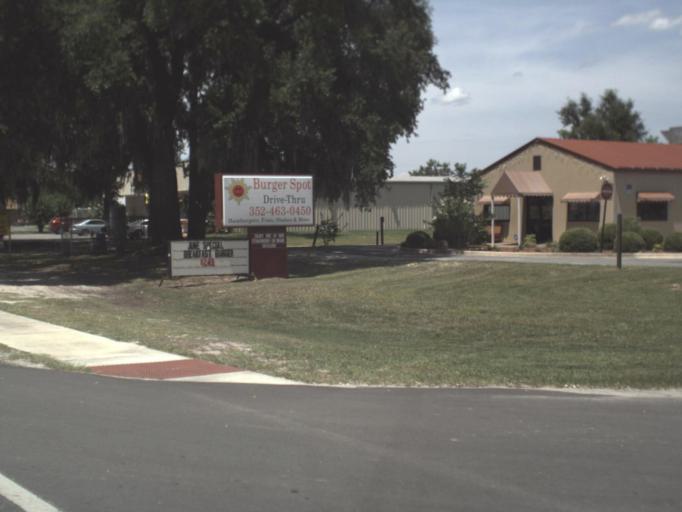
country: US
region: Florida
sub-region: Gilchrist County
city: Trenton
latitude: 29.7633
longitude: -82.8663
